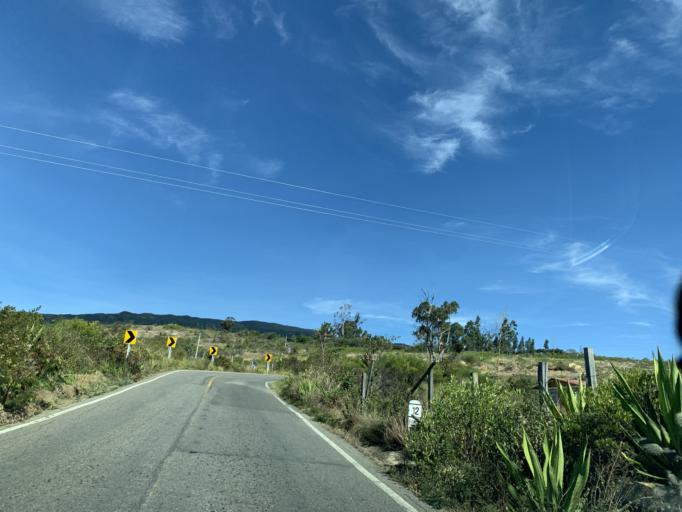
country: CO
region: Boyaca
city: Santa Sofia
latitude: 5.6884
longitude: -73.5884
